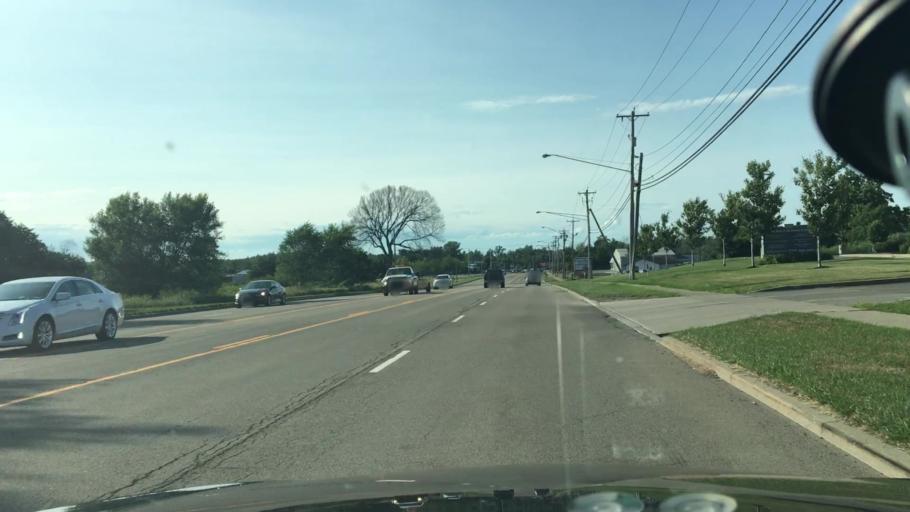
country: US
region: New York
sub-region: Erie County
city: Wanakah
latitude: 42.7538
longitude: -78.8576
